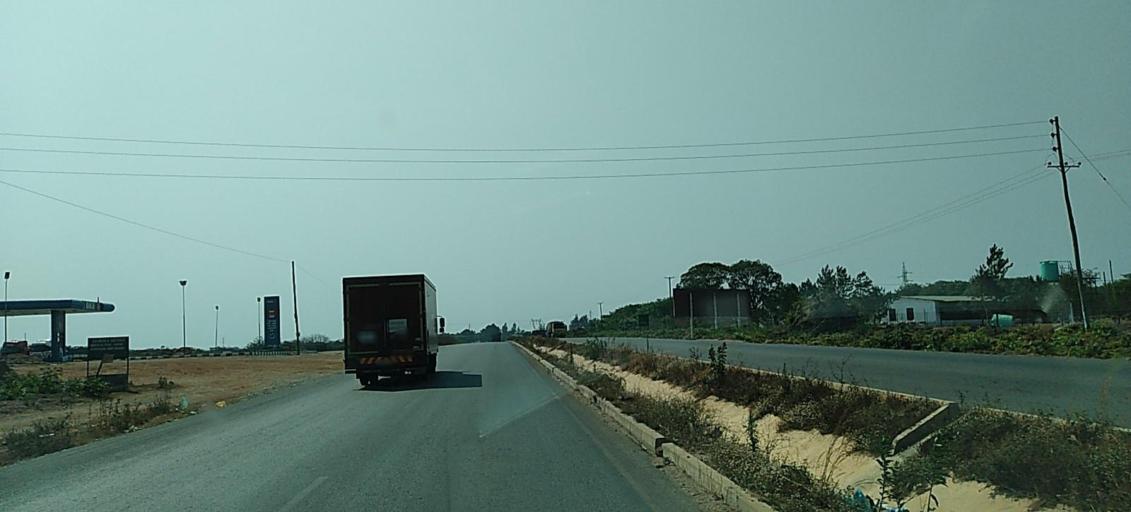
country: ZM
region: Copperbelt
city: Chingola
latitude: -12.5609
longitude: 27.8796
